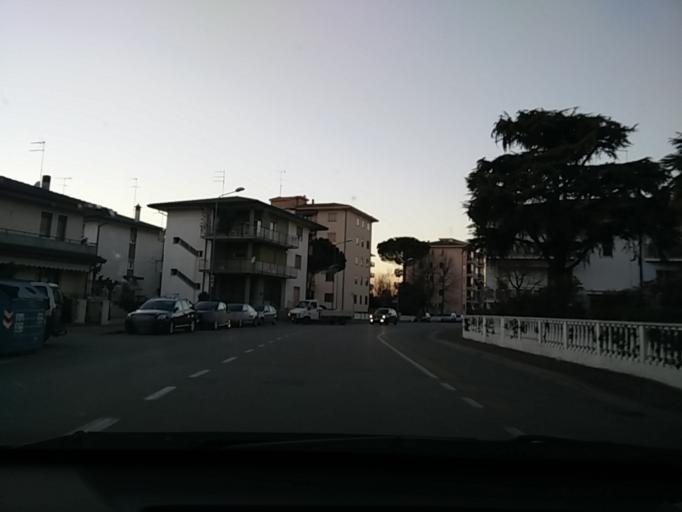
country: IT
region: Veneto
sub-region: Provincia di Venezia
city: San Dona di Piave
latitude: 45.6348
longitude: 12.5805
